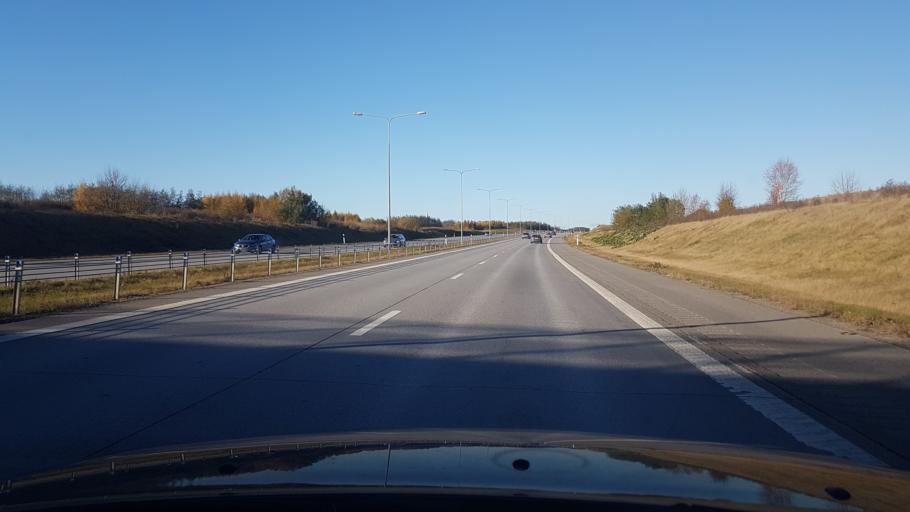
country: SE
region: Uppsala
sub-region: Uppsala Kommun
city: Saevja
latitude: 59.8671
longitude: 17.7108
